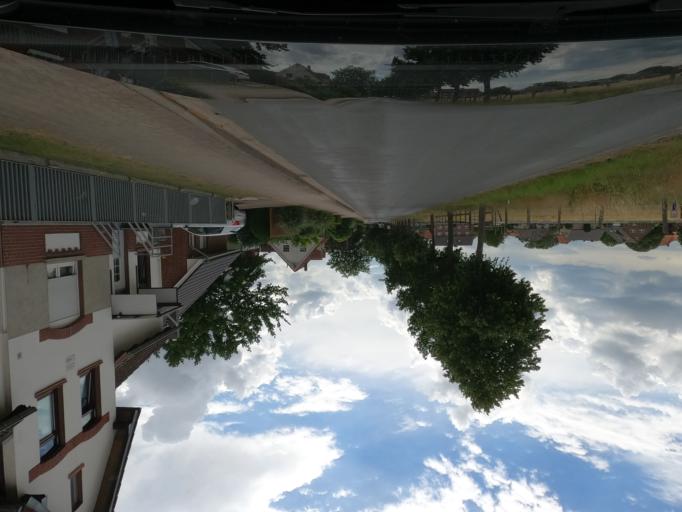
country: DE
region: Lower Saxony
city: Sehnde
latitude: 52.3431
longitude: 9.9101
